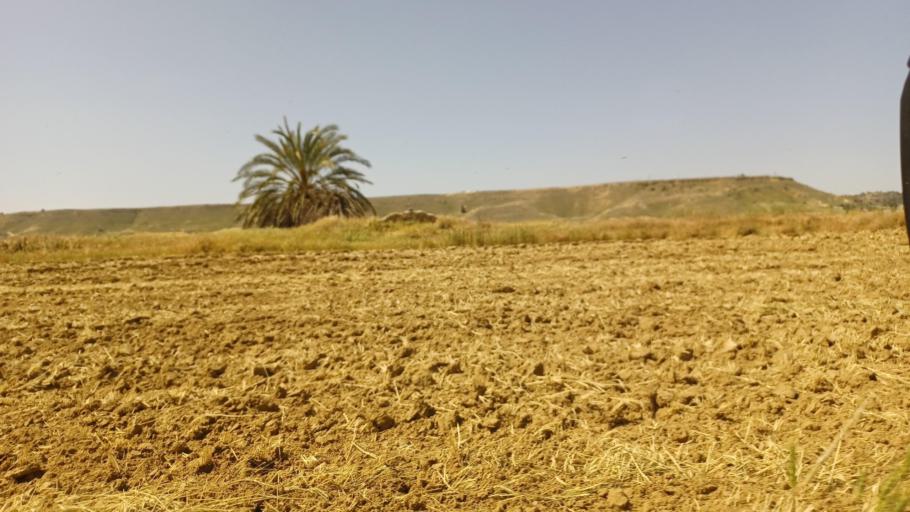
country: CY
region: Lefkosia
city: Mammari
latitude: 35.1812
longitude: 33.2218
